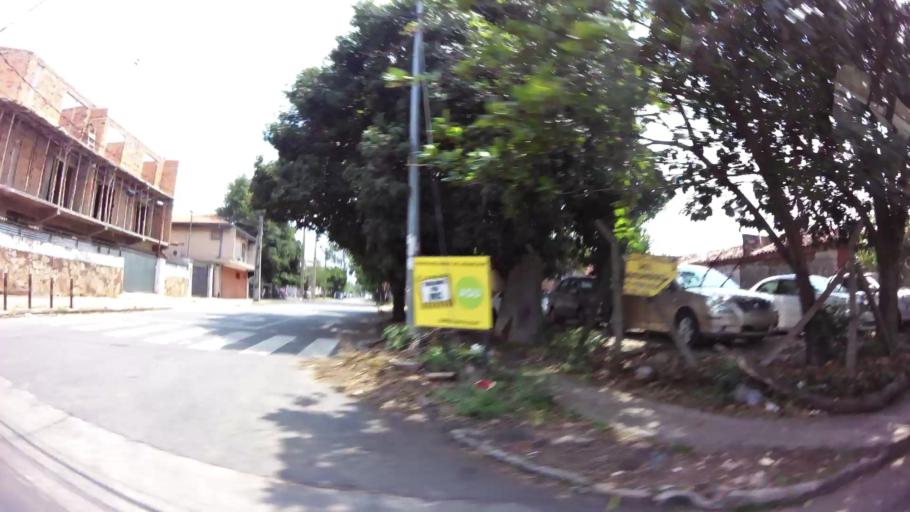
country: PY
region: Central
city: Lambare
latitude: -25.3120
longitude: -57.5705
